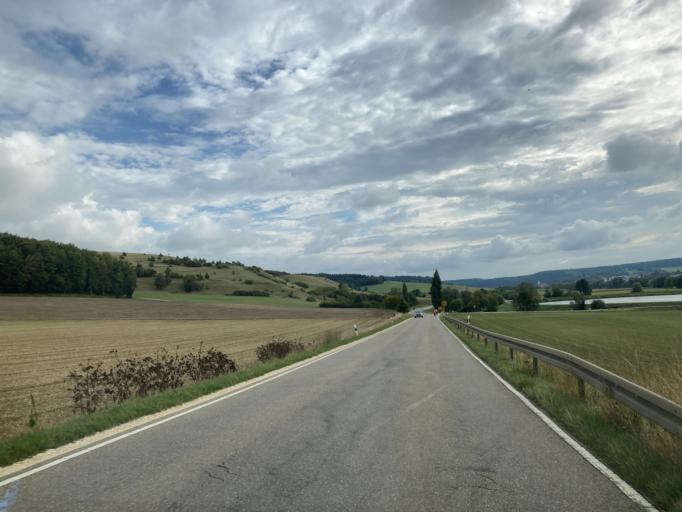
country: DE
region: Baden-Wuerttemberg
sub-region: Regierungsbezirk Stuttgart
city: Dischingen
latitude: 48.7180
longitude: 10.3827
